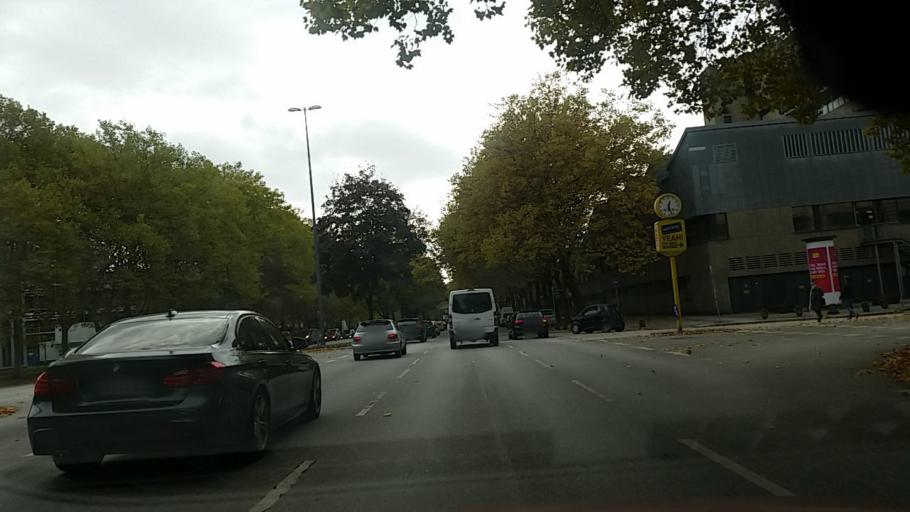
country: DE
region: Hamburg
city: Alsterdorf
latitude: 53.6045
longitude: 10.0250
